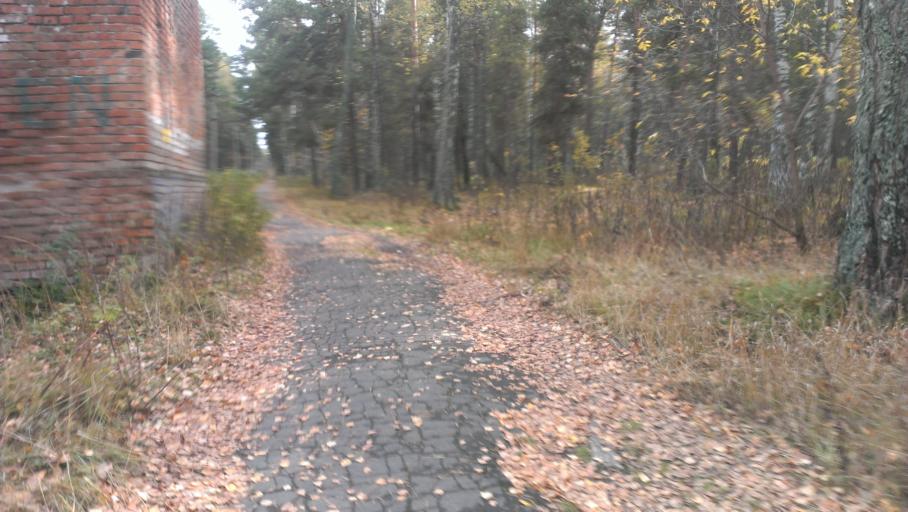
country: RU
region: Altai Krai
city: Yuzhnyy
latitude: 53.2698
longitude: 83.6813
